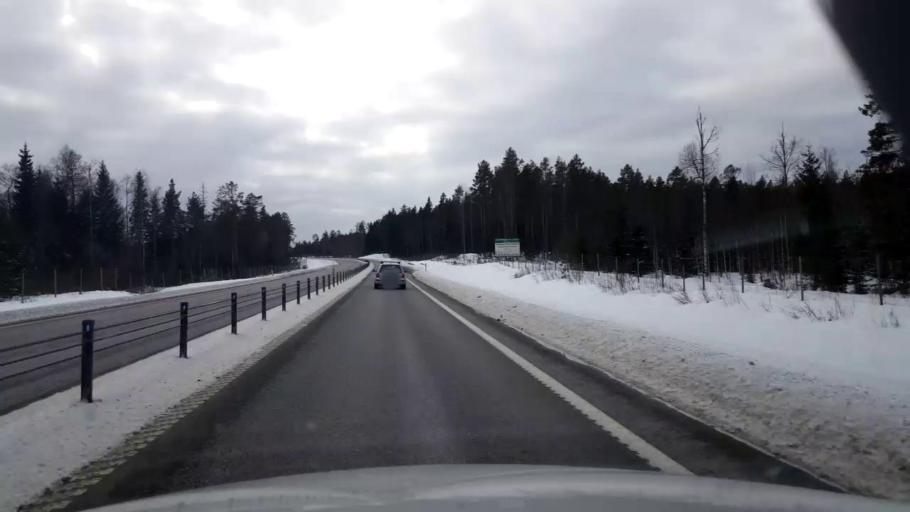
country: SE
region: Vaesternorrland
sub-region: Sundsvalls Kommun
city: Njurundabommen
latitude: 62.1126
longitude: 17.3209
